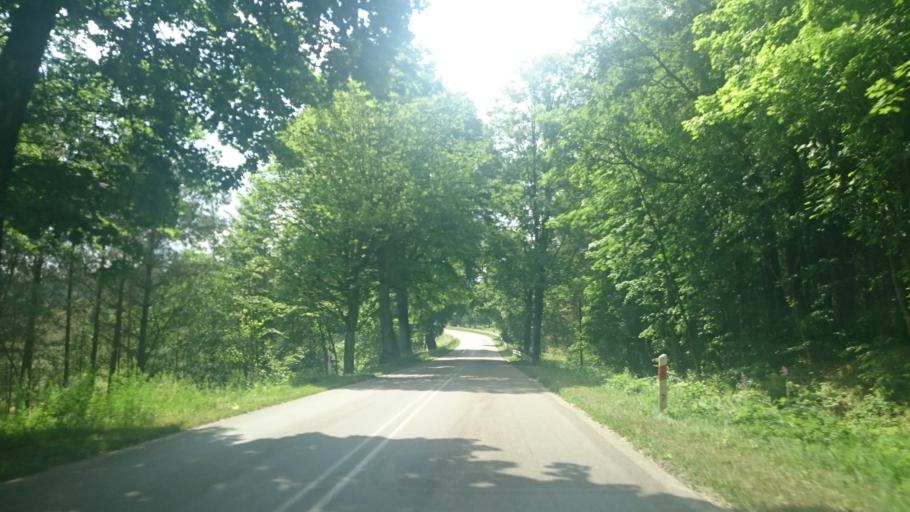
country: PL
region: Pomeranian Voivodeship
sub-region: Powiat starogardzki
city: Kaliska
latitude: 53.9704
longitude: 18.2440
